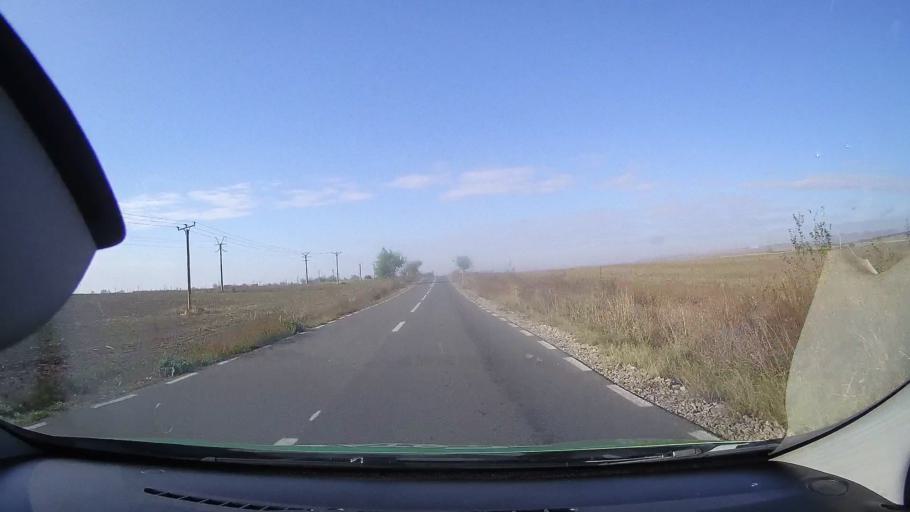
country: RO
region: Tulcea
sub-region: Comuna Murighiol
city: Murighiol
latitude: 45.0278
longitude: 29.1430
